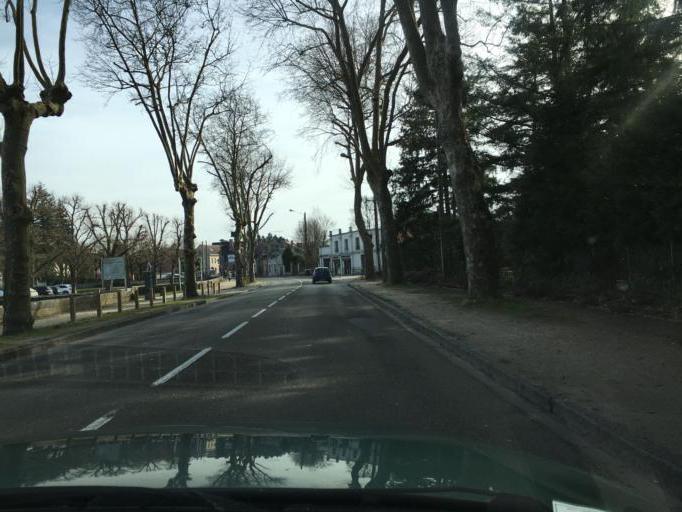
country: FR
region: Centre
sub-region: Departement du Loiret
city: La Ferte-Saint-Aubin
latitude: 47.7262
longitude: 1.9398
